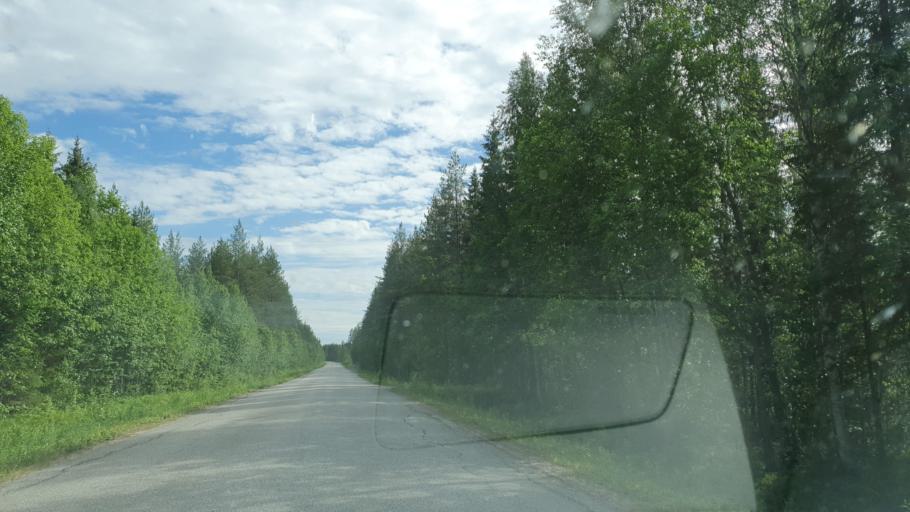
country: FI
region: Kainuu
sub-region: Kehys-Kainuu
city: Suomussalmi
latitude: 64.5771
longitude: 29.1255
